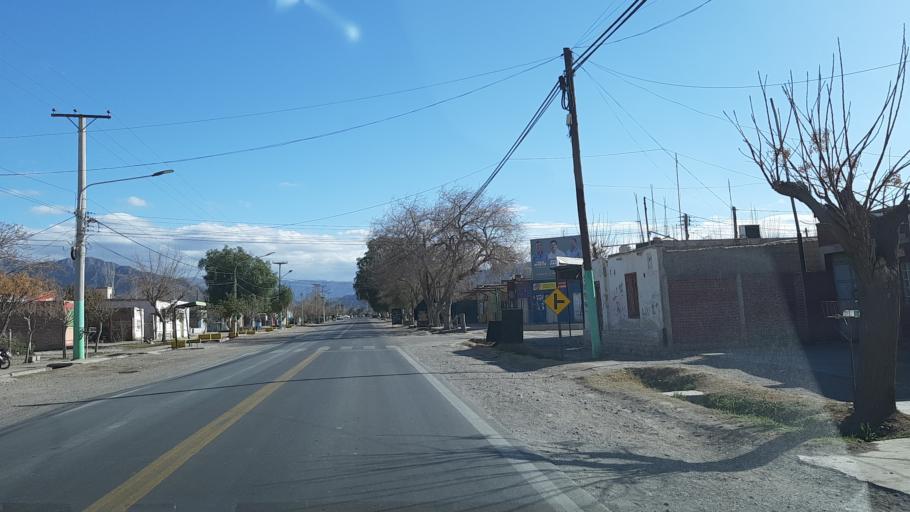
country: AR
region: San Juan
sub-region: Departamento de Rivadavia
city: Rivadavia
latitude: -31.5403
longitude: -68.6213
